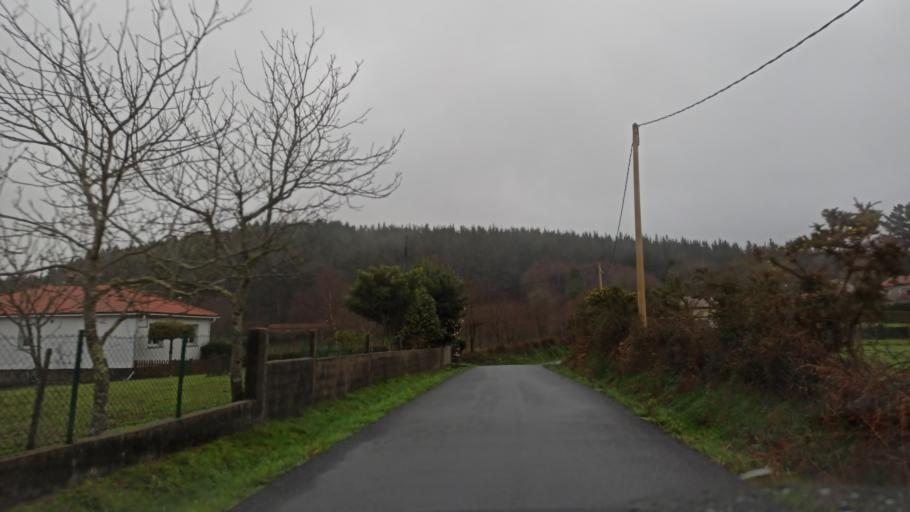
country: ES
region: Galicia
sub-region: Provincia da Coruna
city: Cesuras
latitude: 43.1806
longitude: -8.1466
